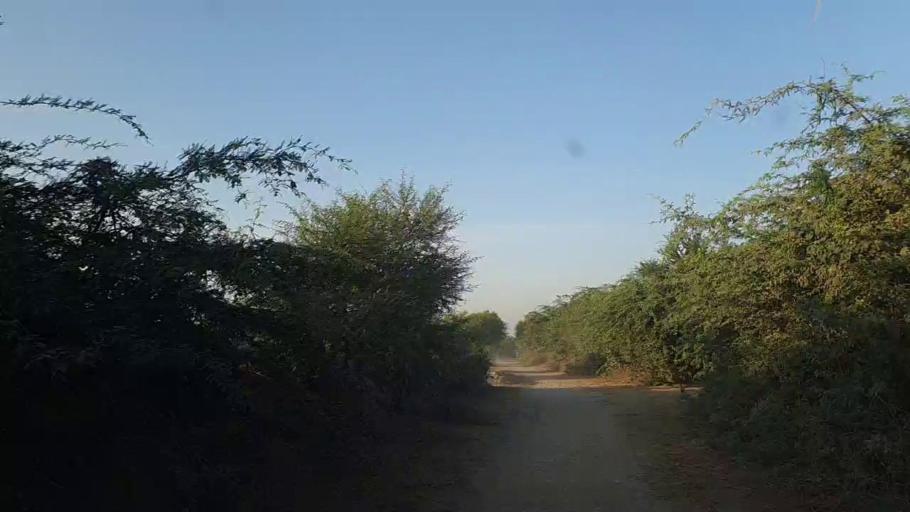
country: PK
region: Sindh
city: Mirpur Batoro
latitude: 24.7192
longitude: 68.2140
